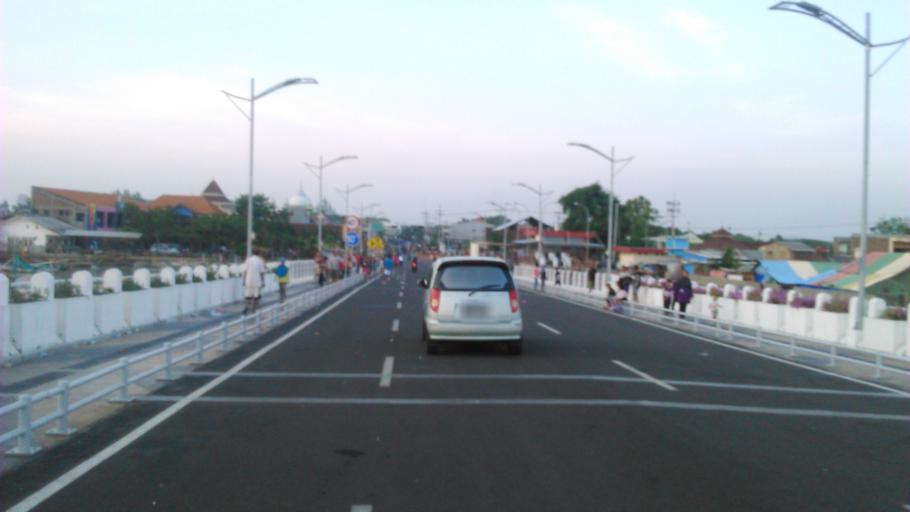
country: ID
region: East Java
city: Labansari
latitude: -7.2393
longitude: 112.7974
